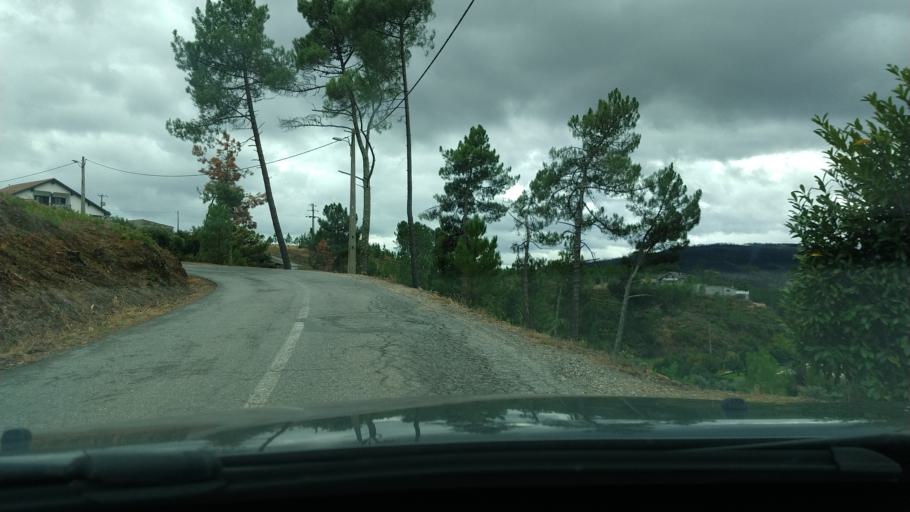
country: PT
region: Castelo Branco
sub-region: Concelho do Fundao
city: Aldeia de Joanes
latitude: 40.2230
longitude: -7.6408
